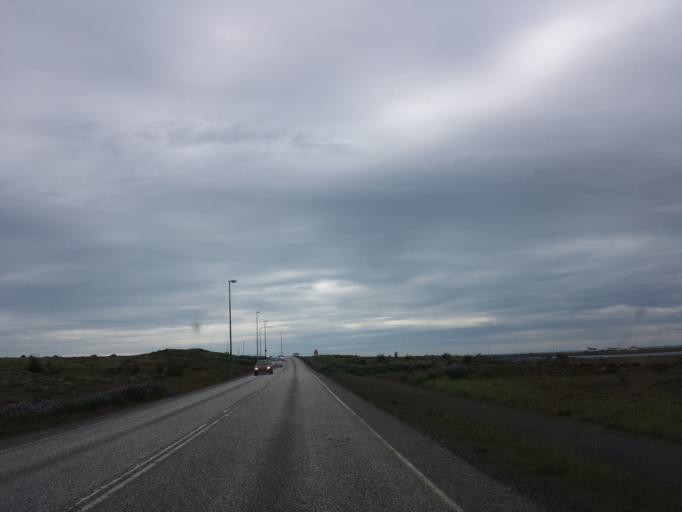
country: IS
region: Capital Region
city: Alftanes
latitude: 64.0876
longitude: -21.9779
